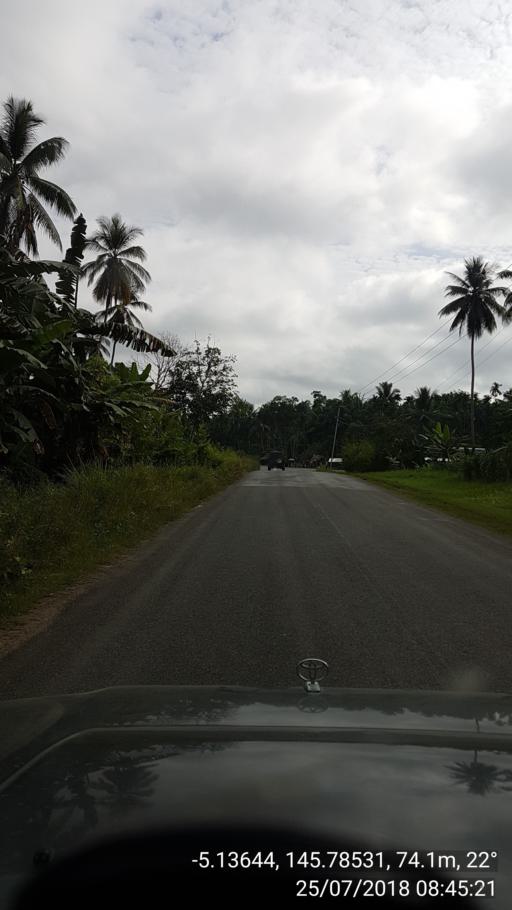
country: PG
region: Madang
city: Madang
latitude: -5.1367
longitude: 145.7853
